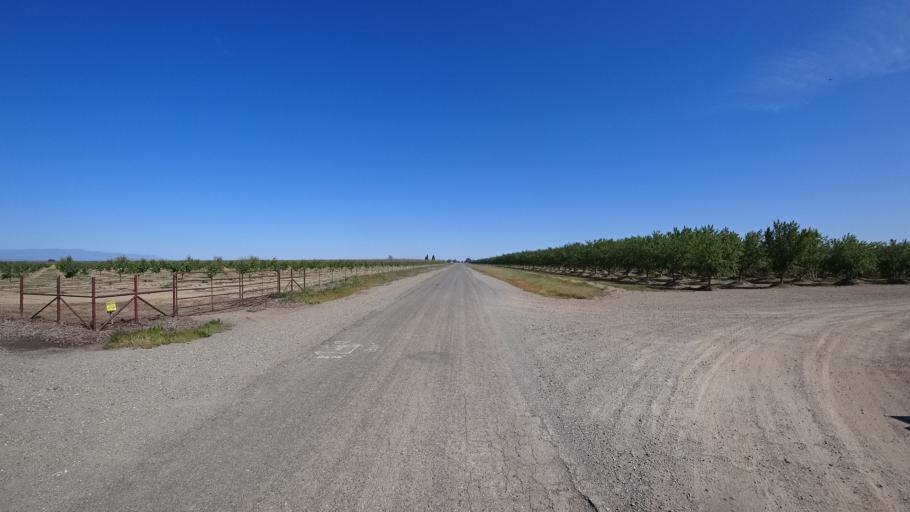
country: US
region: California
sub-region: Glenn County
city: Willows
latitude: 39.6311
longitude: -122.1600
